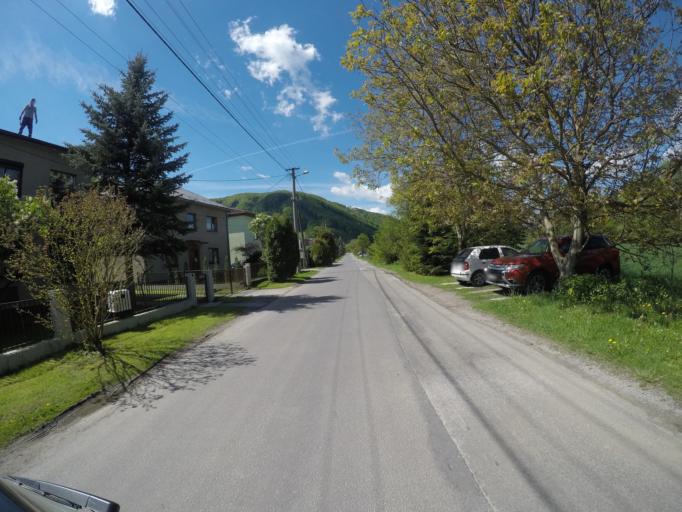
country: SK
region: Banskobystricky
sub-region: Okres Banska Bystrica
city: Banska Bystrica
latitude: 48.7371
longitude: 19.2066
